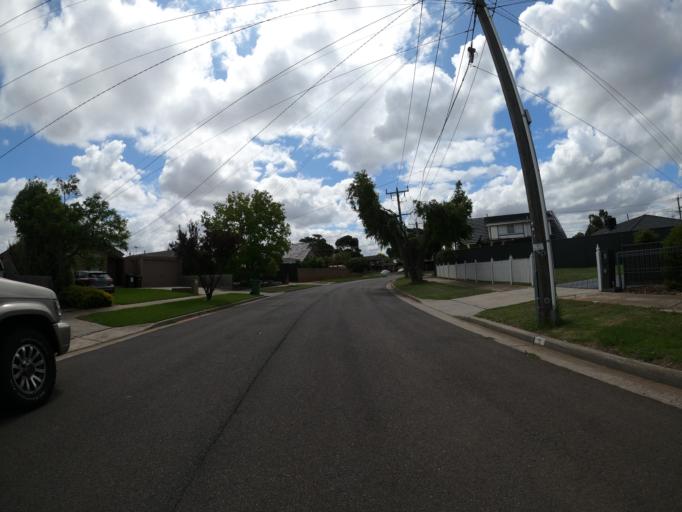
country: AU
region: Victoria
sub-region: Hume
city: Westmeadows
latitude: -37.6805
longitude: 144.8756
